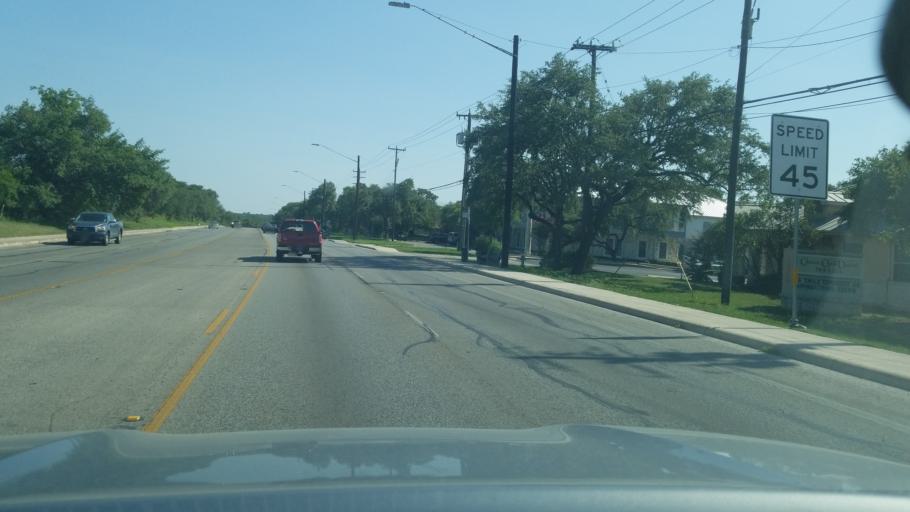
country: US
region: Texas
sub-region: Bexar County
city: Hollywood Park
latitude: 29.5963
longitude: -98.5108
